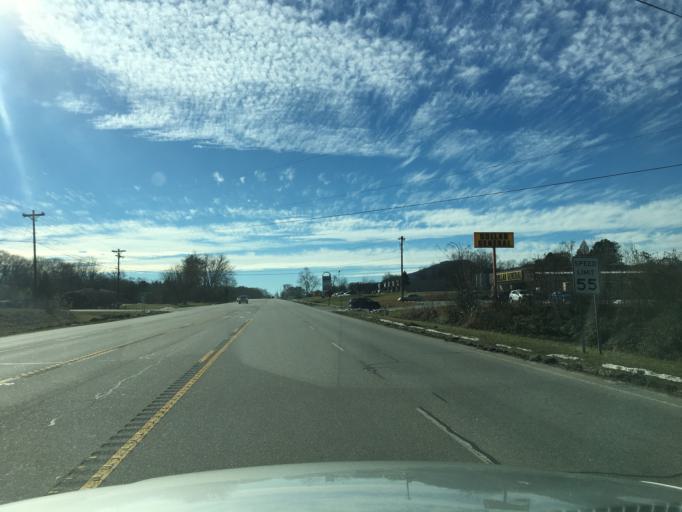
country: US
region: North Carolina
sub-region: Henderson County
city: Mills River
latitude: 35.3839
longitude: -82.5698
